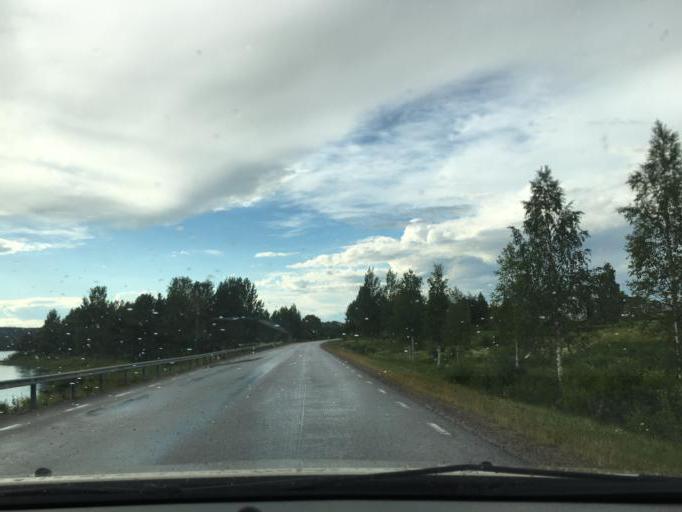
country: SE
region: Norrbotten
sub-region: Kalix Kommun
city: Toere
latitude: 66.0047
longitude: 22.8525
